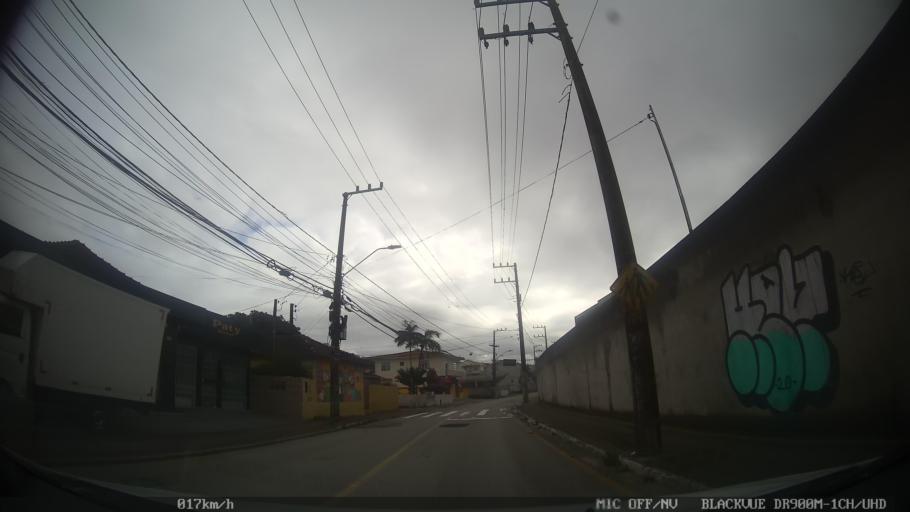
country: BR
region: Santa Catarina
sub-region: Sao Jose
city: Campinas
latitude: -27.5962
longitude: -48.6233
